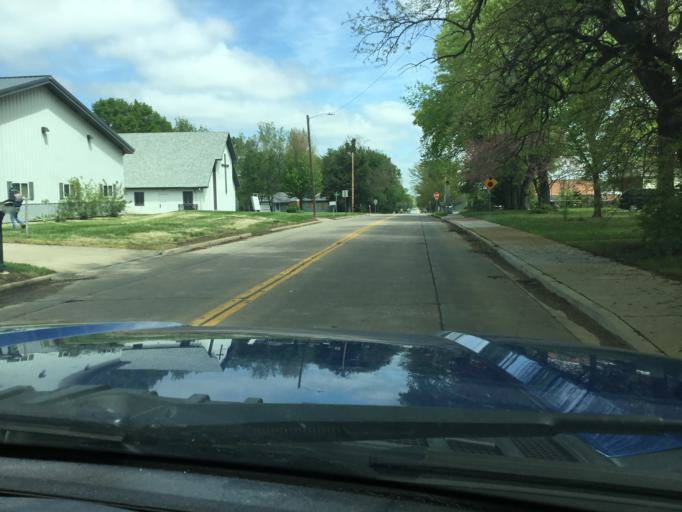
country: US
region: Kansas
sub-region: Shawnee County
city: Topeka
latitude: 39.0162
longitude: -95.6609
